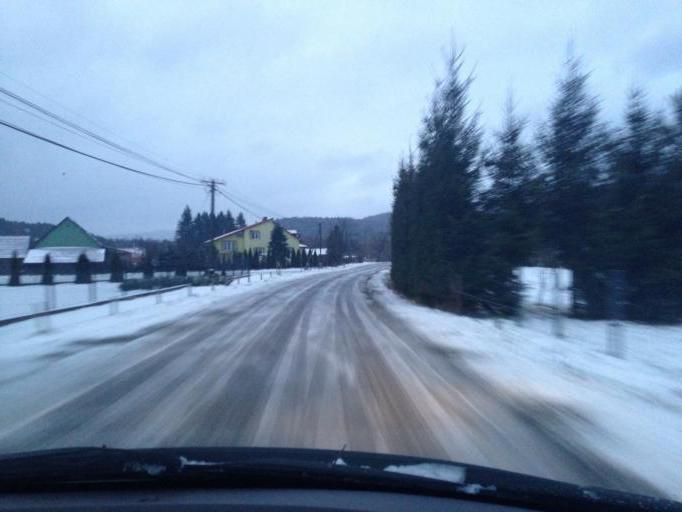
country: PL
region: Subcarpathian Voivodeship
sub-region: Powiat jasielski
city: Krempna
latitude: 49.5081
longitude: 21.5114
